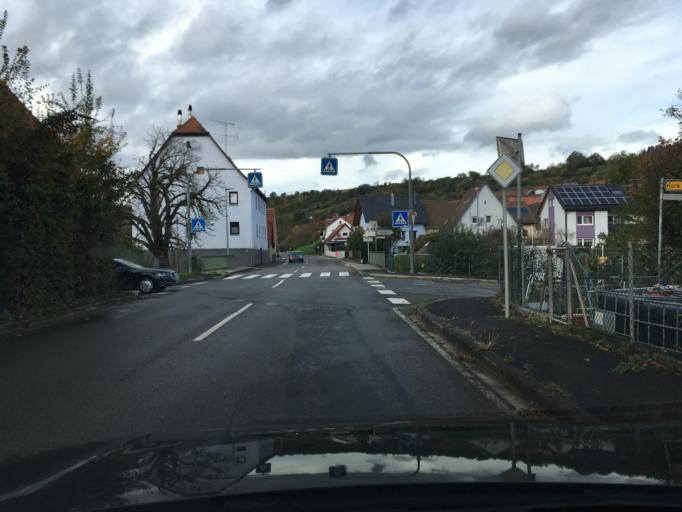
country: DE
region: Baden-Wuerttemberg
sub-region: Regierungsbezirk Stuttgart
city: Mockmuhl
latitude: 49.3184
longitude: 9.3792
